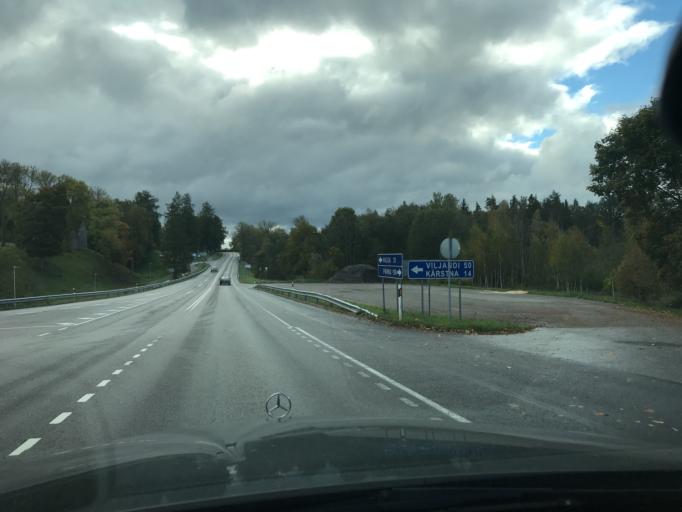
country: EE
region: Valgamaa
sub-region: Torva linn
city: Torva
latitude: 58.0179
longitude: 25.8766
